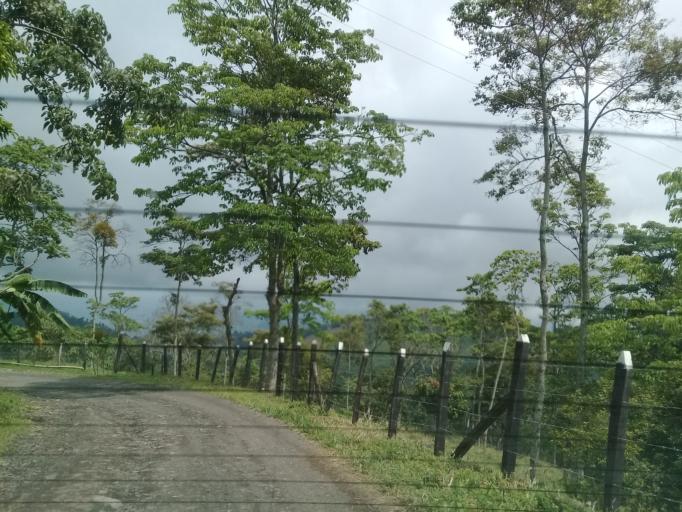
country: CO
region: Cundinamarca
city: Quipile
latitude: 4.7155
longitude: -74.5423
